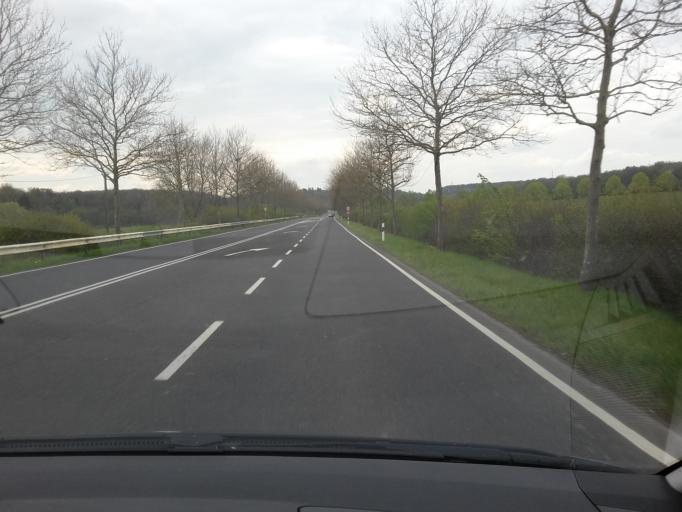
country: LU
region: Luxembourg
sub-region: Canton de Luxembourg
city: Bertrange
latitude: 49.5939
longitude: 6.0247
